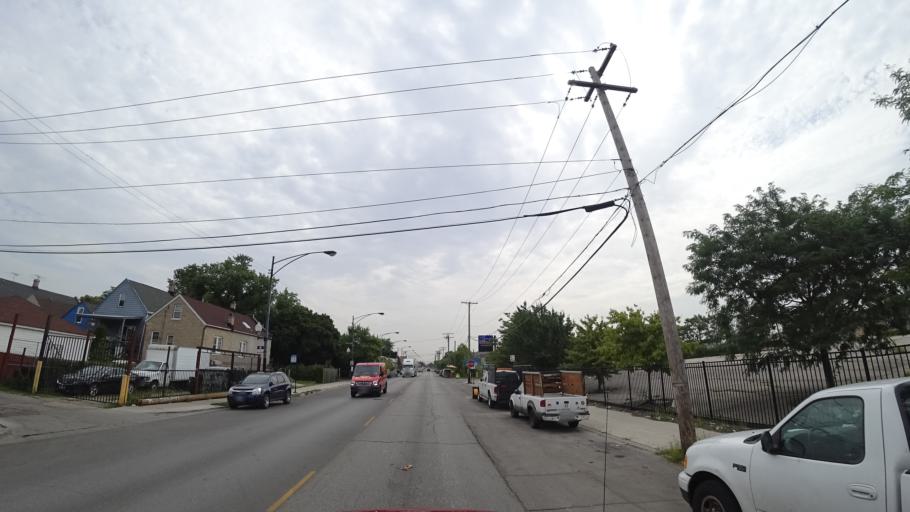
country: US
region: Illinois
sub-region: Cook County
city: Cicero
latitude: 41.8371
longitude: -87.7130
